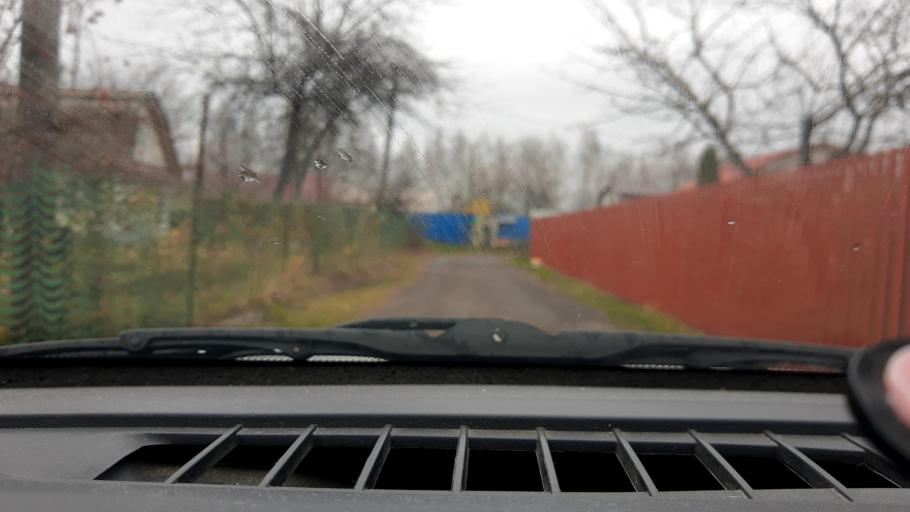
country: RU
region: Nizjnij Novgorod
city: Gorbatovka
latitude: 56.3860
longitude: 43.8129
